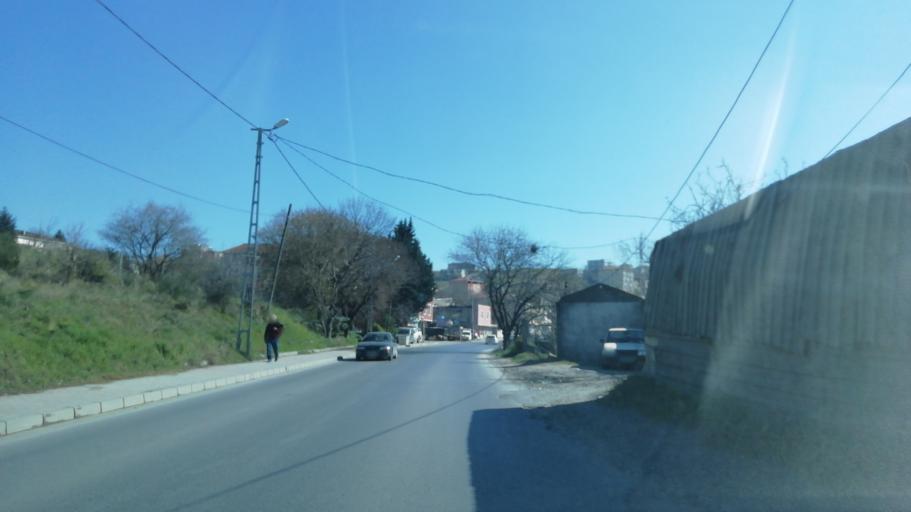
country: TR
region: Istanbul
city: Basaksehir
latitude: 41.0559
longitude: 28.7495
